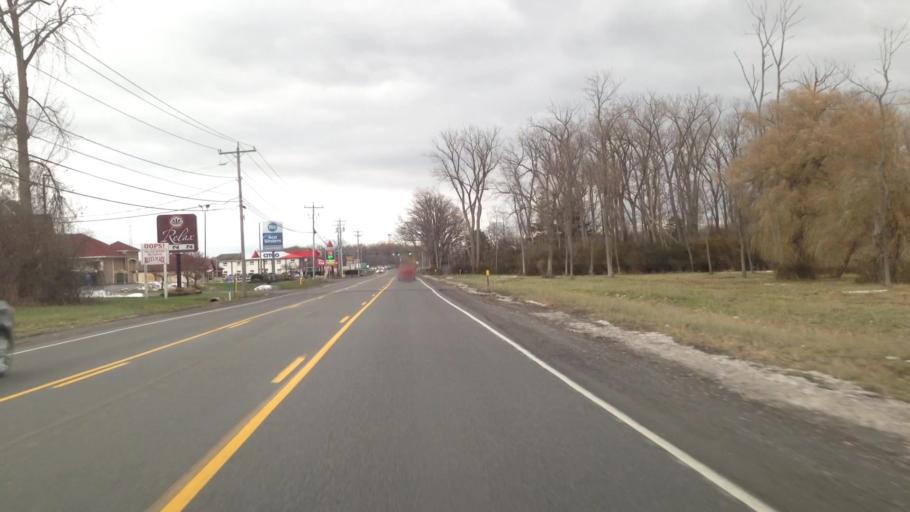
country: US
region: New York
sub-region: Genesee County
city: Batavia
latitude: 43.0166
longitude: -78.1965
